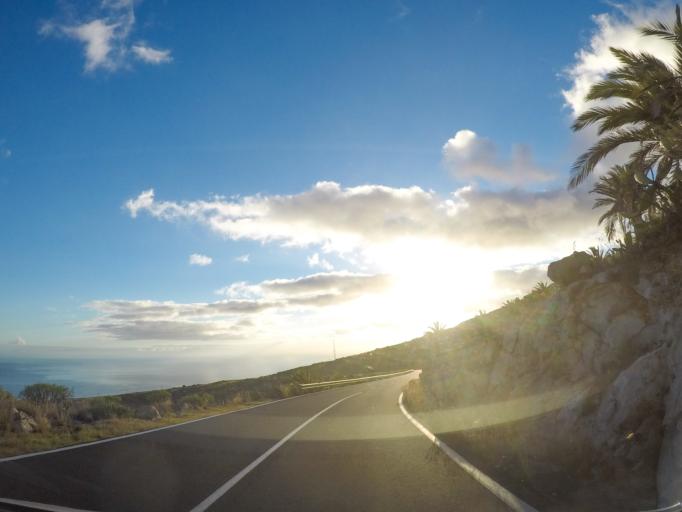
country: ES
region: Canary Islands
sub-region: Provincia de Santa Cruz de Tenerife
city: Alajero
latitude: 28.0546
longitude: -17.2302
